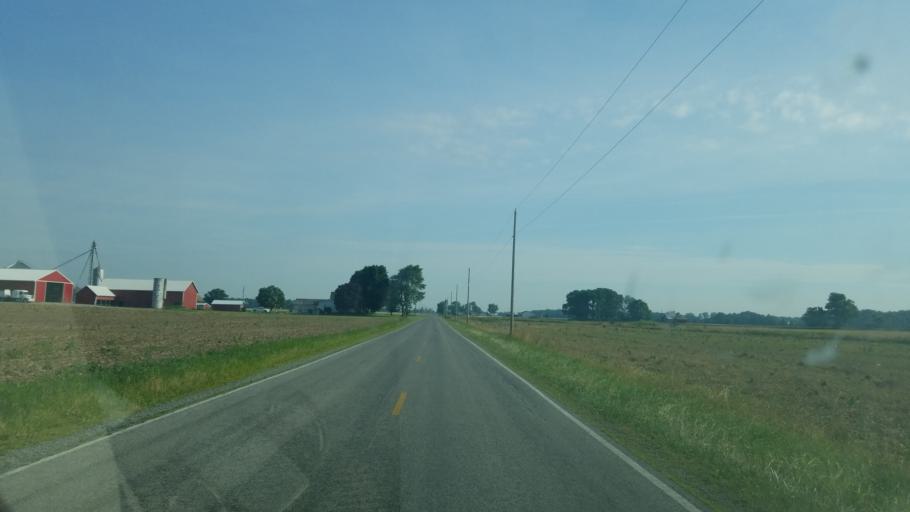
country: US
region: Ohio
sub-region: Hancock County
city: Arlington
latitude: 40.9225
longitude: -83.6986
